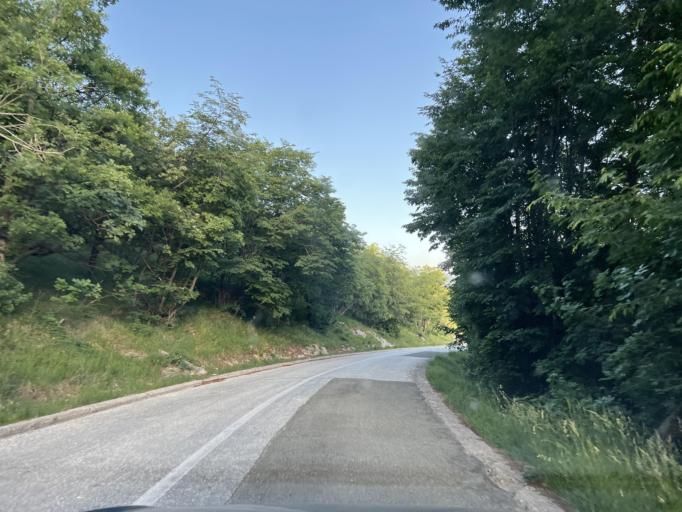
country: HR
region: Primorsko-Goranska
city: Skrljevo
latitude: 45.3860
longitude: 14.5642
